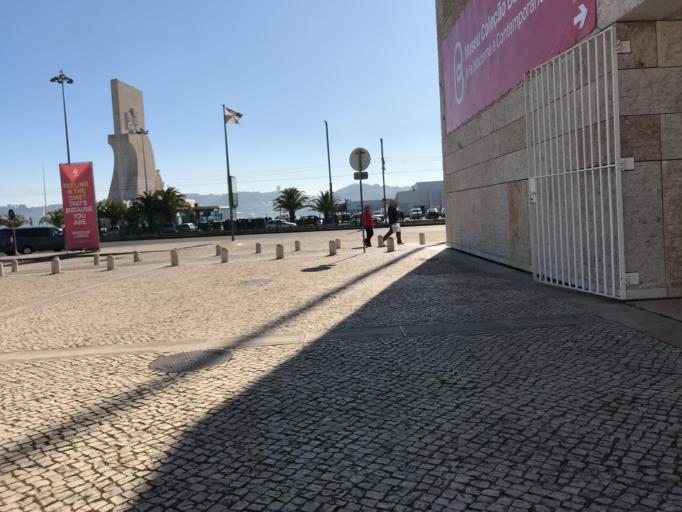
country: PT
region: Lisbon
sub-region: Oeiras
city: Alges
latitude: 38.6953
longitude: -9.2073
